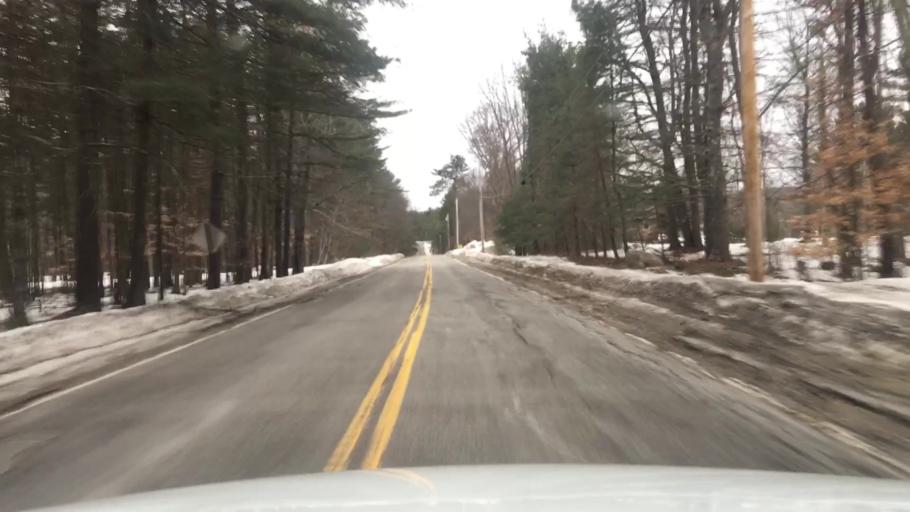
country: US
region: Maine
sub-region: York County
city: Shapleigh
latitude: 43.5528
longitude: -70.8542
